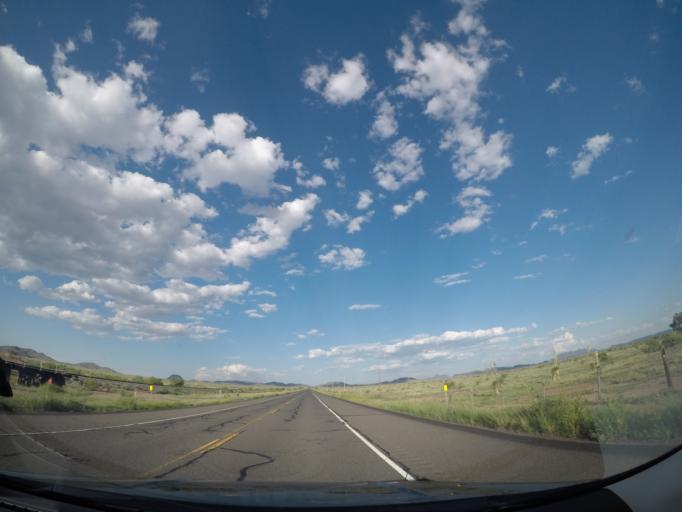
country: US
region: Texas
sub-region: Presidio County
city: Marfa
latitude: 30.2754
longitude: -103.8783
